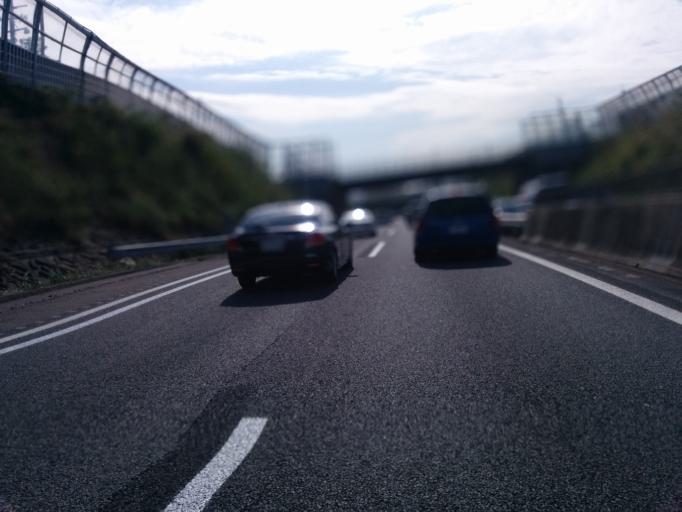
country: JP
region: Mie
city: Komono
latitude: 34.9848
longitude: 136.5320
